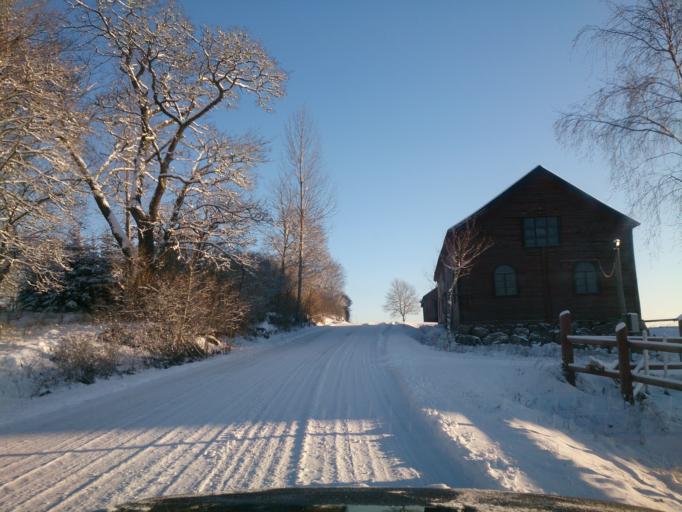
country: SE
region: OEstergoetland
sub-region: Norrkopings Kommun
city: Krokek
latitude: 58.5219
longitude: 16.5009
